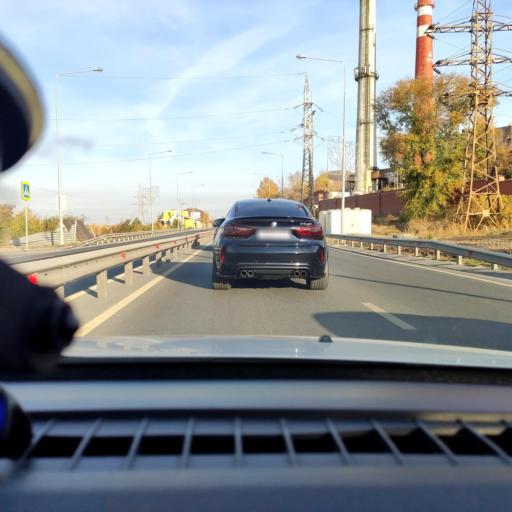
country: RU
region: Samara
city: Volzhskiy
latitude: 53.3780
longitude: 50.1707
